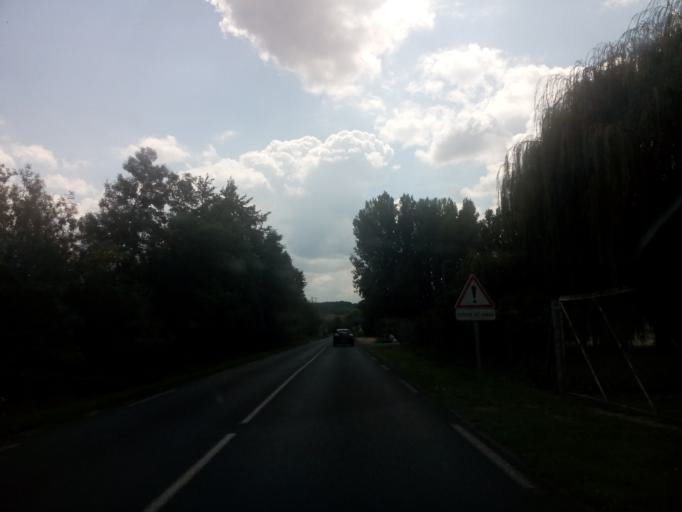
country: FR
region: Centre
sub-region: Departement d'Indre-et-Loire
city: Langeais
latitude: 47.3035
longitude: 0.4130
